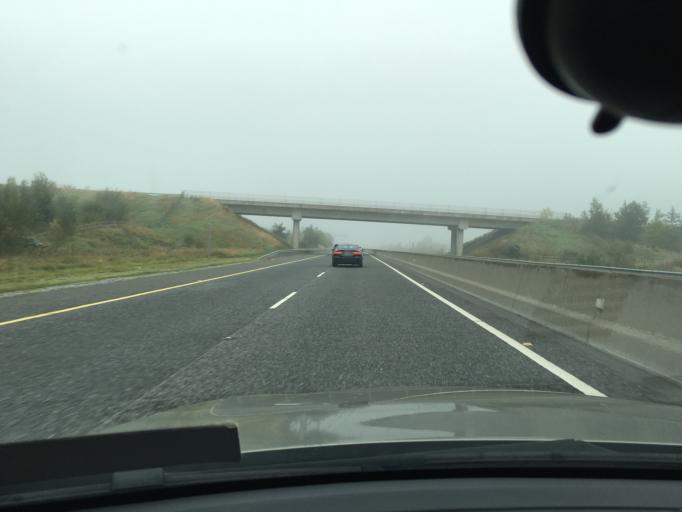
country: IE
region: Leinster
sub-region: An Iarmhi
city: Moate
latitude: 53.3969
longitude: -7.8166
